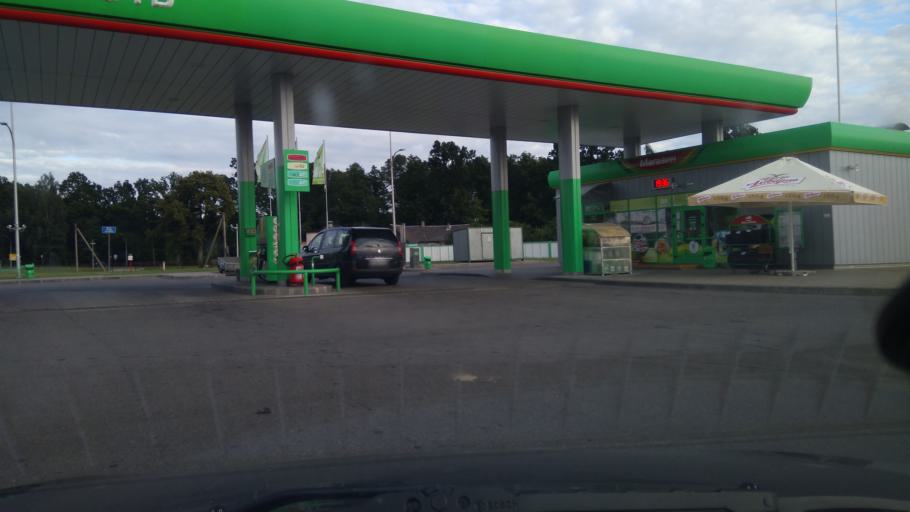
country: BY
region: Grodnenskaya
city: Masty
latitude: 53.4185
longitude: 24.5652
